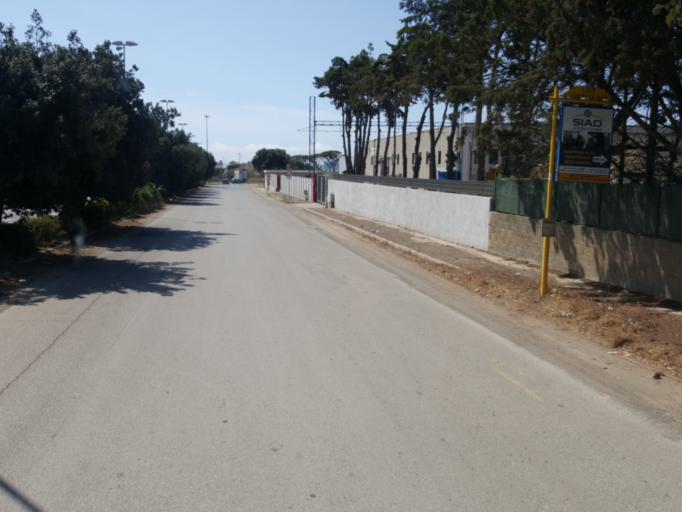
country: IT
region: Latium
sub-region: Citta metropolitana di Roma Capitale
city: Aurelia
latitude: 42.1181
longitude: 11.7786
